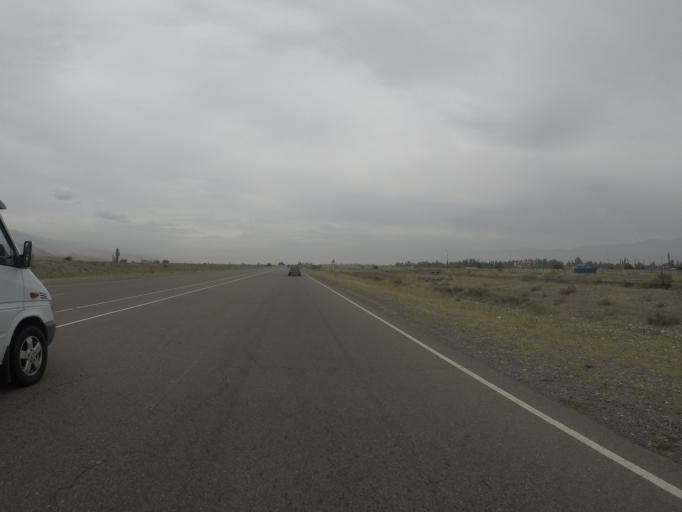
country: KG
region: Chuy
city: Bystrovka
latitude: 42.8295
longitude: 75.5232
